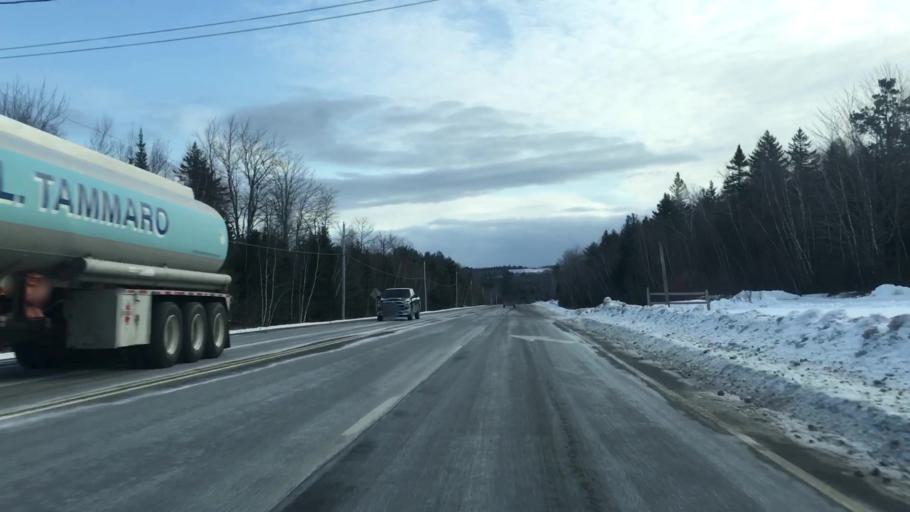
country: US
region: Maine
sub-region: Washington County
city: Machias
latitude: 44.9487
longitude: -67.6948
